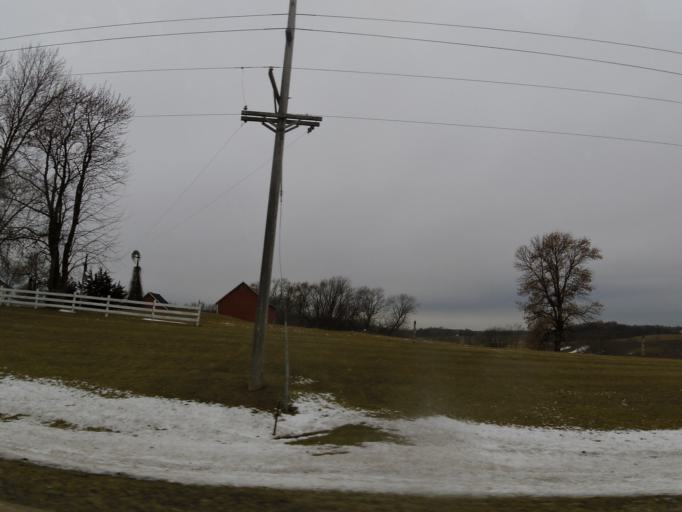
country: US
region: Minnesota
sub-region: Carver County
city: Watertown
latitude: 44.9453
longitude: -93.8334
